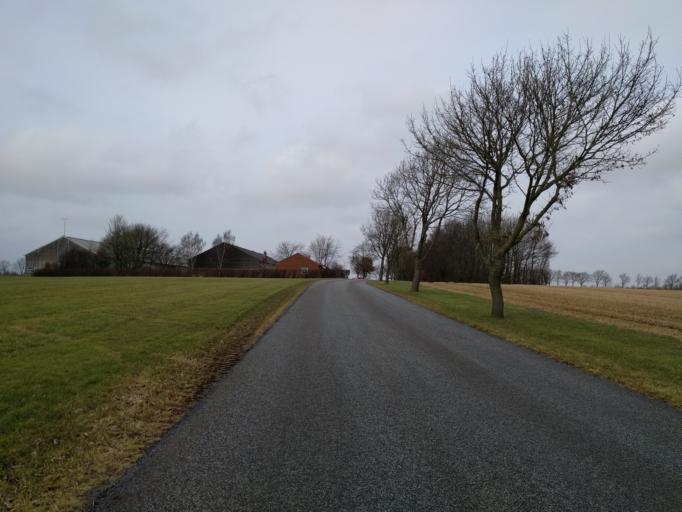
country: DK
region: Central Jutland
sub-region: Viborg Kommune
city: Bjerringbro
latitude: 56.4932
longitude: 9.5721
